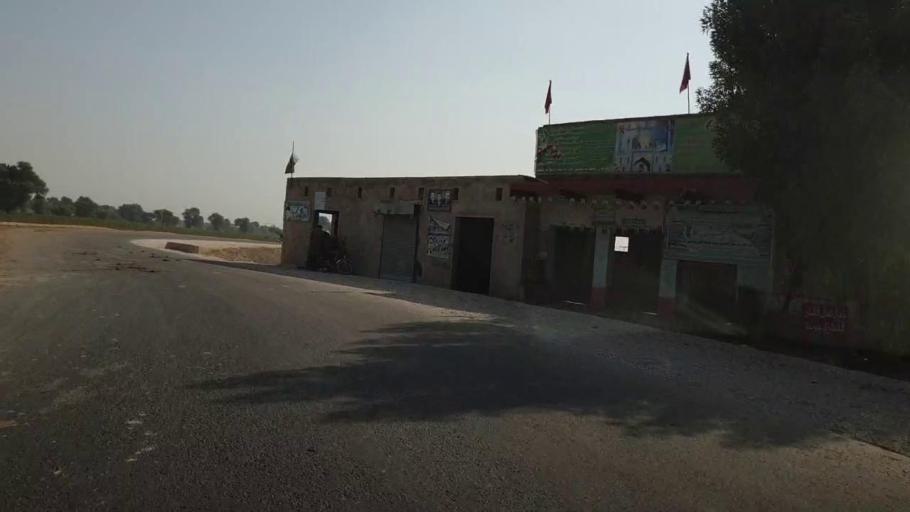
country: PK
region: Sindh
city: Dadu
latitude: 26.6752
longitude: 67.7763
